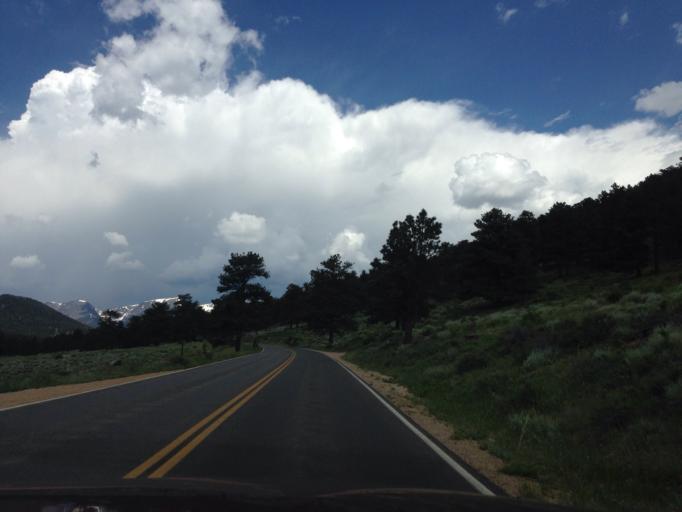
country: US
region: Colorado
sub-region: Larimer County
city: Estes Park
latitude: 40.3734
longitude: -105.5921
